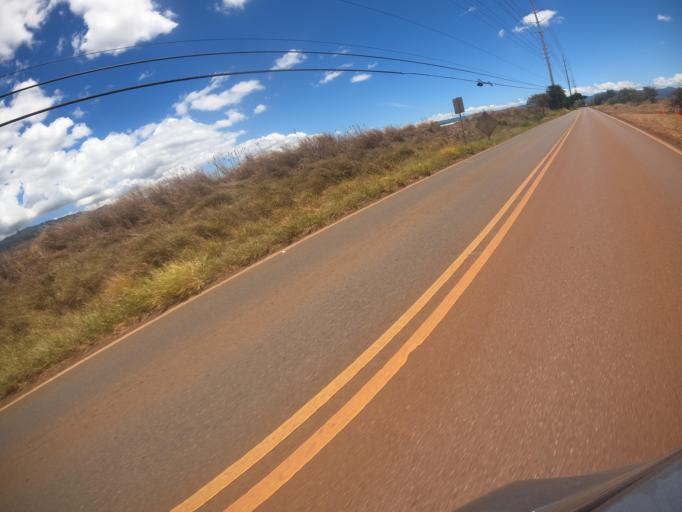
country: US
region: Hawaii
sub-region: Honolulu County
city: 'Ewa Villages
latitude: 21.3687
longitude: -158.0496
